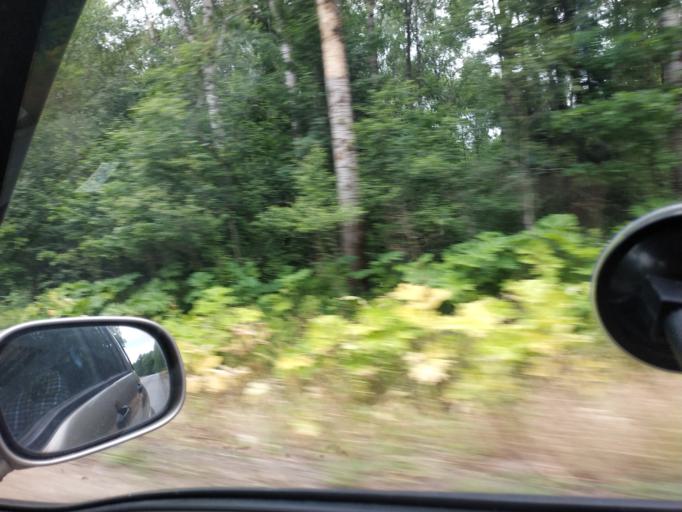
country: RU
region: Moskovskaya
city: Krasnoarmeysk
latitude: 56.0769
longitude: 38.2446
